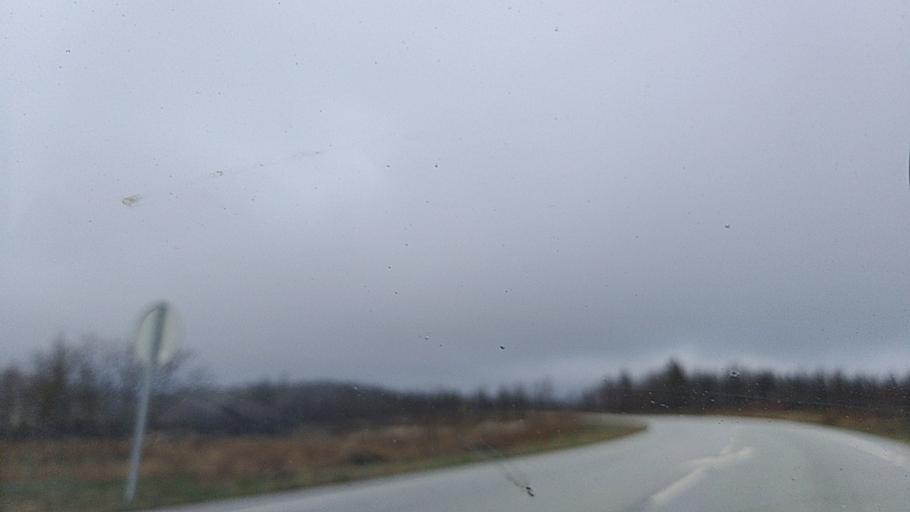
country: PT
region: Guarda
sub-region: Fornos de Algodres
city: Fornos de Algodres
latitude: 40.7009
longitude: -7.4797
